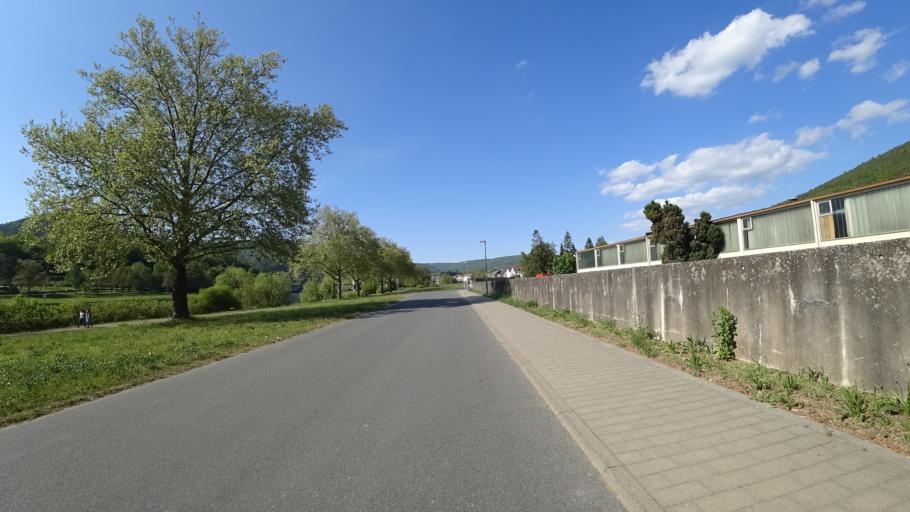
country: DE
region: Baden-Wuerttemberg
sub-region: Regierungsbezirk Stuttgart
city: Freudenberg
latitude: 49.7481
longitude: 9.3246
